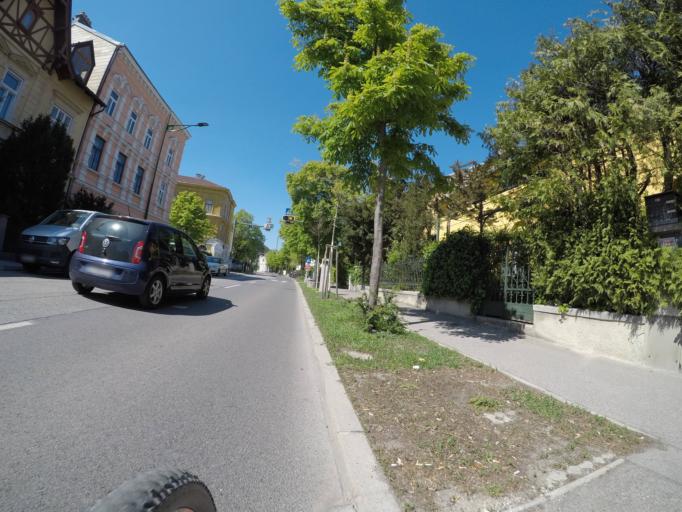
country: AT
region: Lower Austria
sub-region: Politischer Bezirk Modling
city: Modling
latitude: 48.0830
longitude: 16.2906
